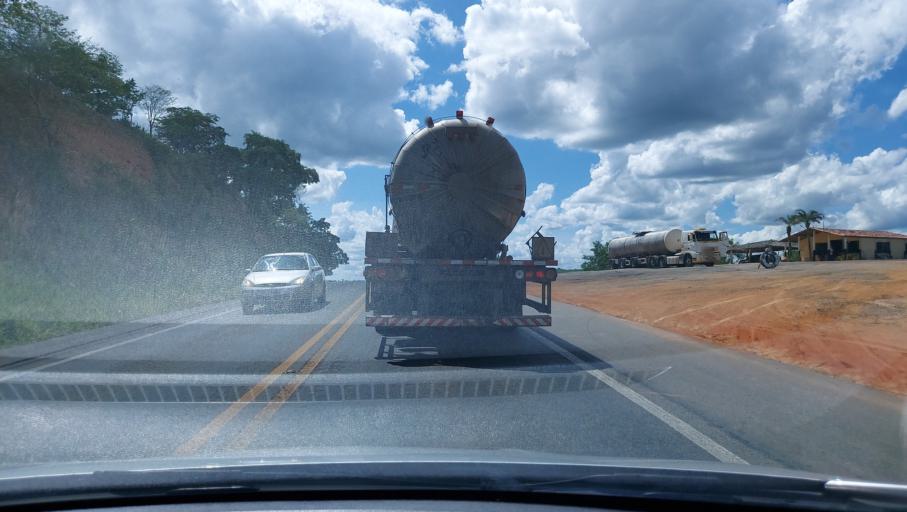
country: BR
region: Bahia
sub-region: Ruy Barbosa
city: Terra Nova
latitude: -12.4497
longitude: -40.6062
